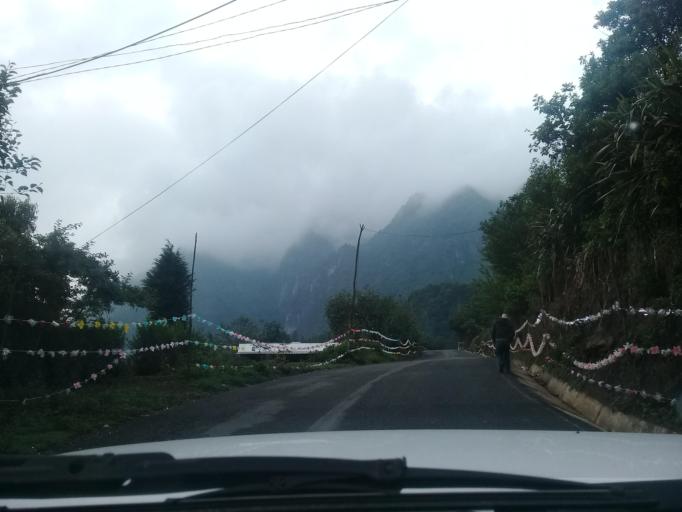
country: MX
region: Veracruz
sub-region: Mariano Escobedo
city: San Isidro el Berro
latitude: 18.9535
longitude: -97.1954
